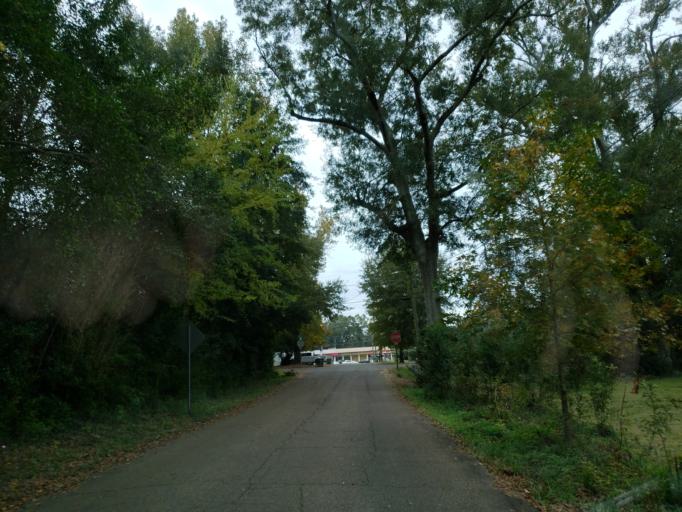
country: US
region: Mississippi
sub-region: Forrest County
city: Hattiesburg
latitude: 31.3262
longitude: -89.3089
